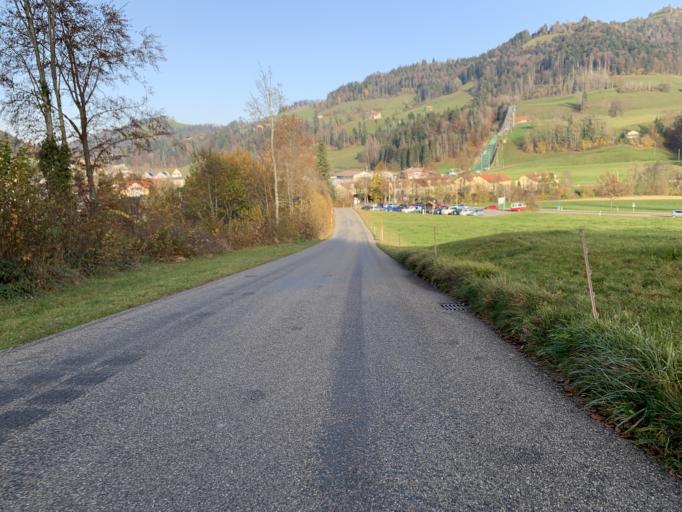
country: CH
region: Zurich
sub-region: Bezirk Hinwil
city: Wald
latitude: 47.3106
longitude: 8.9112
